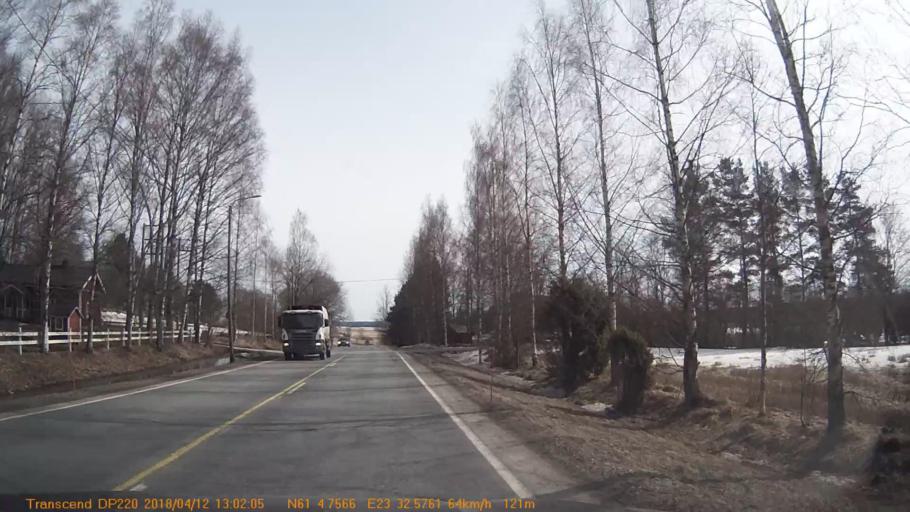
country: FI
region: Pirkanmaa
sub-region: Etelae-Pirkanmaa
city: Urjala
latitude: 61.0792
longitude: 23.5433
